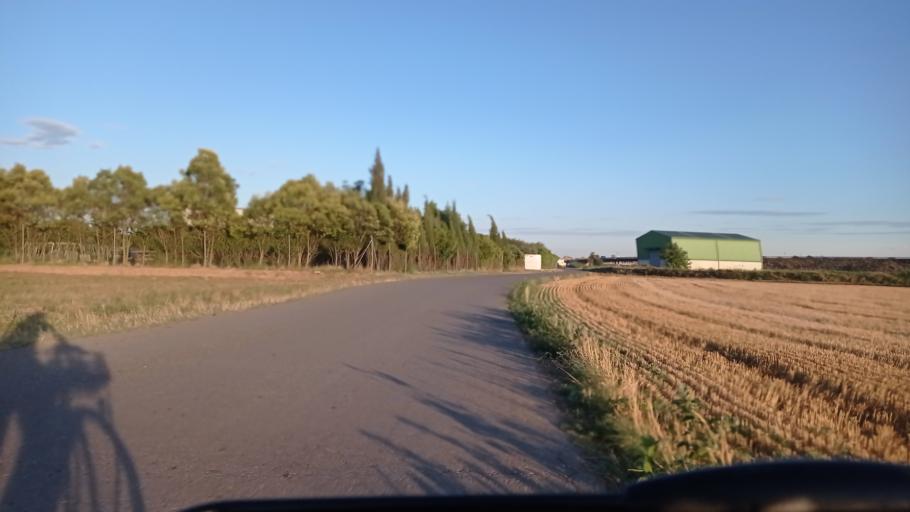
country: ES
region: Aragon
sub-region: Provincia de Zaragoza
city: Oliver-Valdefierro, Oliver, Valdefierro
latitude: 41.6825
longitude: -0.9345
